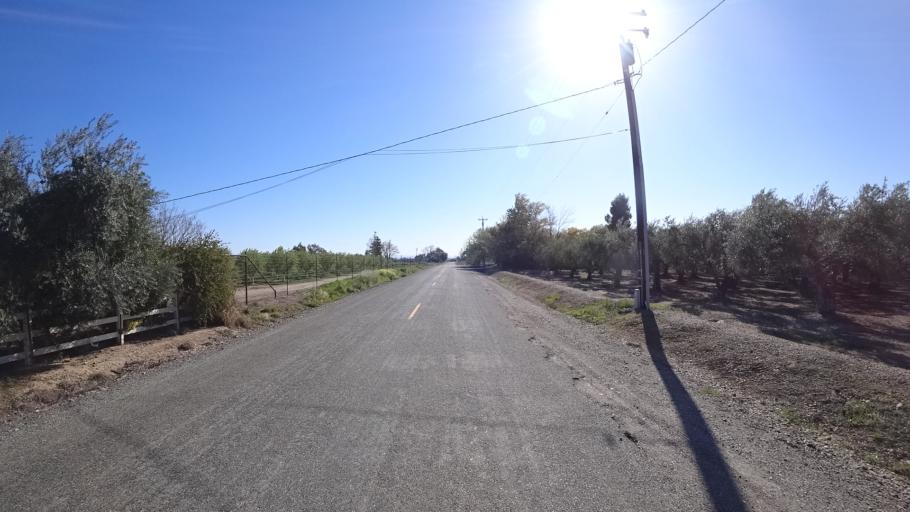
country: US
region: California
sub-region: Glenn County
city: Orland
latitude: 39.7476
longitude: -122.2216
